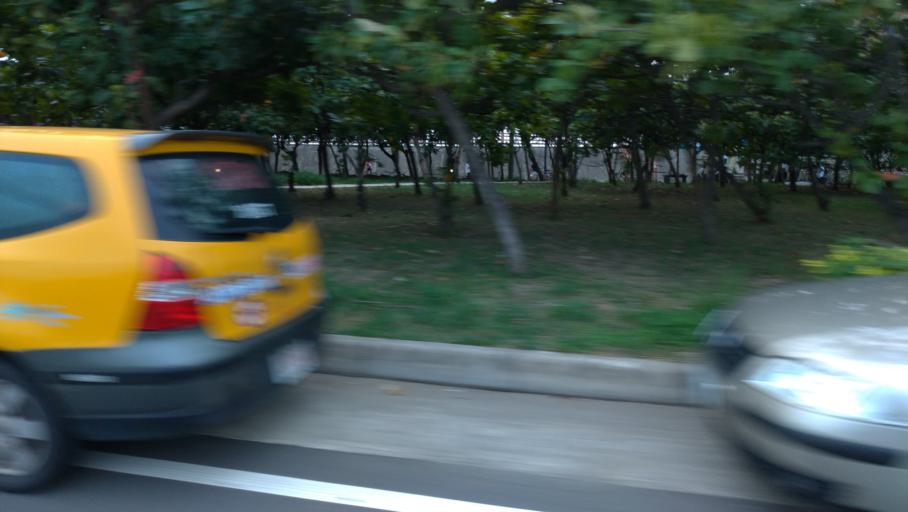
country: TW
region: Taiwan
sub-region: Hsinchu
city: Hsinchu
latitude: 24.7832
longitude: 120.9154
